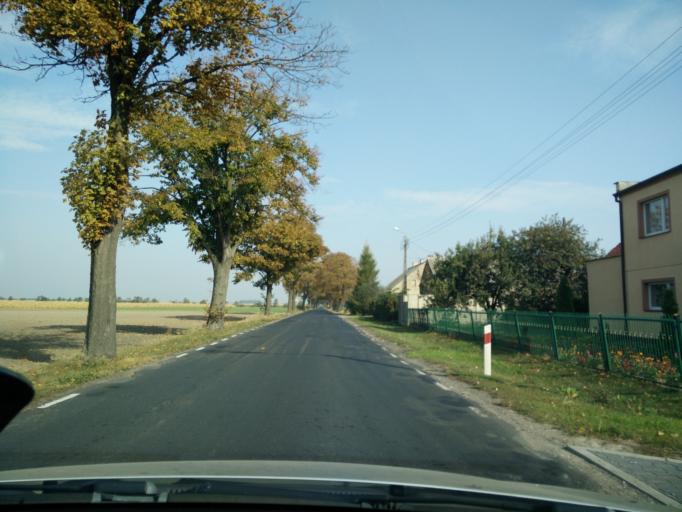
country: PL
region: Greater Poland Voivodeship
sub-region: Powiat sredzki
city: Sroda Wielkopolska
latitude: 52.2516
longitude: 17.2972
